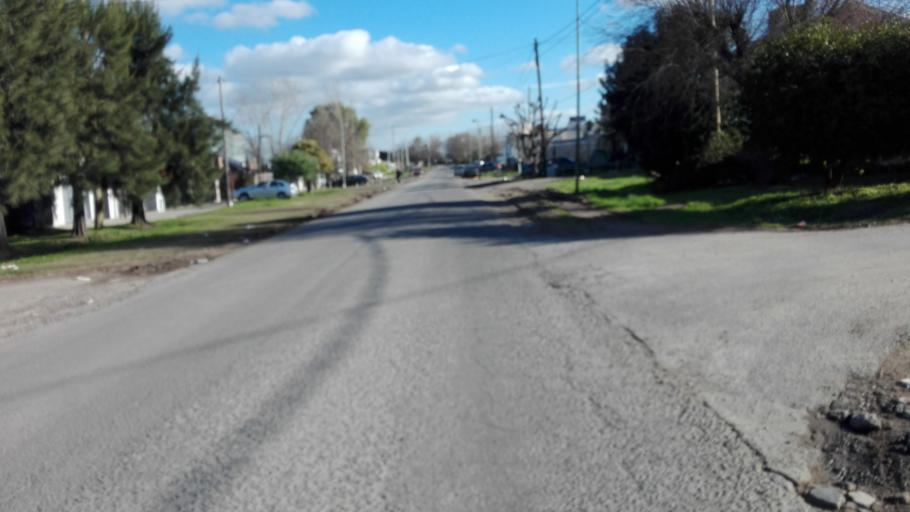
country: AR
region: Buenos Aires
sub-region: Partido de La Plata
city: La Plata
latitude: -34.9037
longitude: -58.0217
